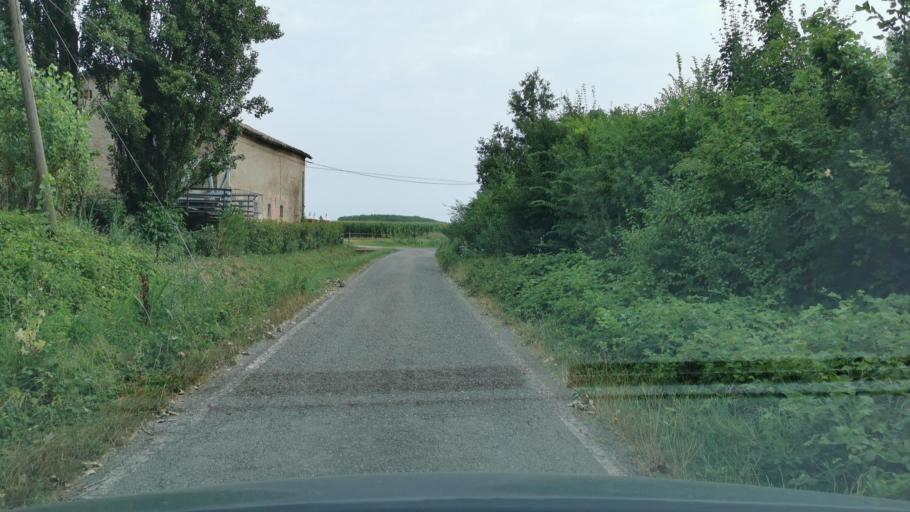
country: IT
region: Emilia-Romagna
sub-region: Provincia di Modena
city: Villanova
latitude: 44.6970
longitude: 10.9056
